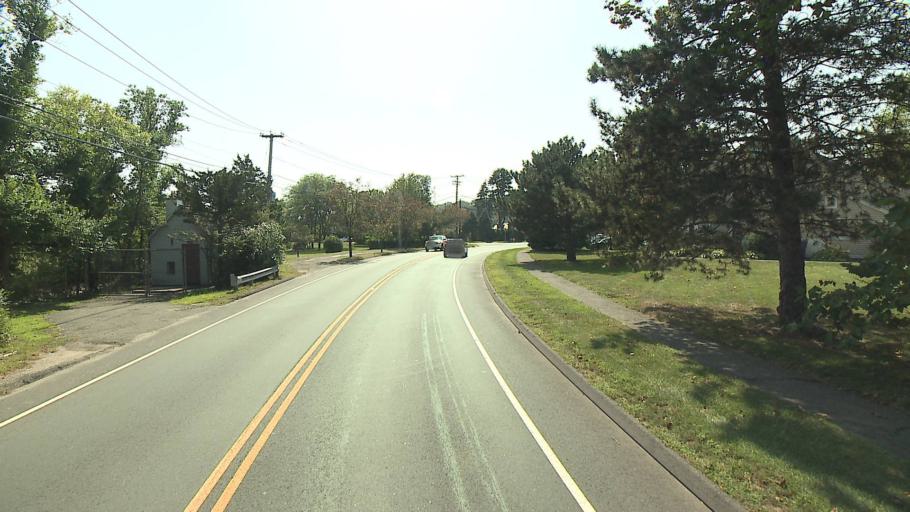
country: US
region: Connecticut
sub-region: Fairfield County
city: Westport
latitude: 41.1481
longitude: -73.3632
